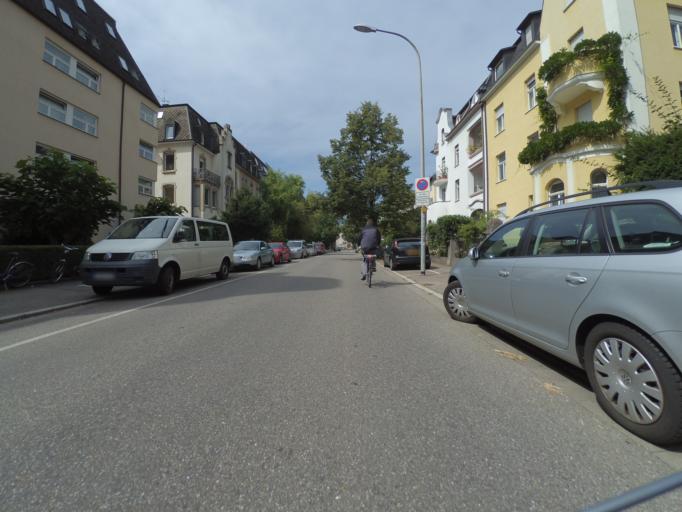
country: DE
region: Baden-Wuerttemberg
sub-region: Freiburg Region
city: Freiburg
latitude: 47.9918
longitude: 7.8585
